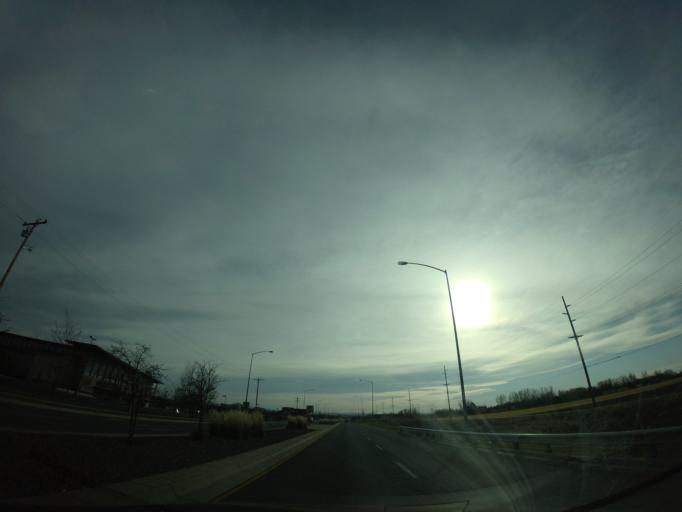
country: US
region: Montana
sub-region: Yellowstone County
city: Billings
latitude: 45.7756
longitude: -108.6177
